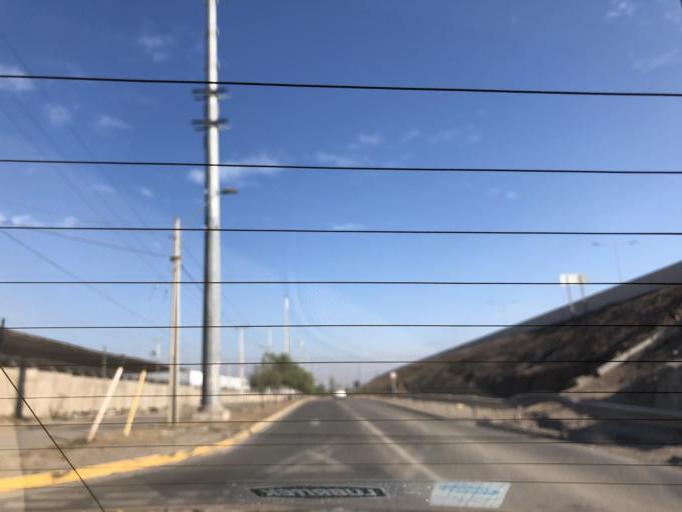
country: CL
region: Santiago Metropolitan
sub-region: Provincia de Santiago
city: La Pintana
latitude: -33.6350
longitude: -70.6249
